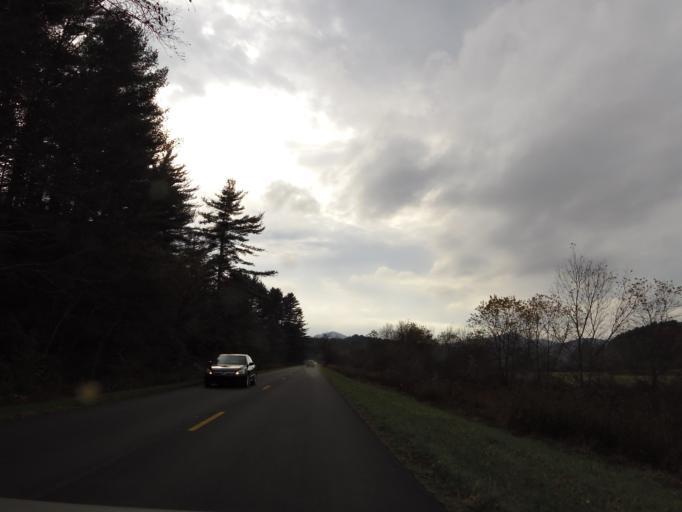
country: US
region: North Carolina
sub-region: Alleghany County
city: Sparta
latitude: 36.3933
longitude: -81.2324
